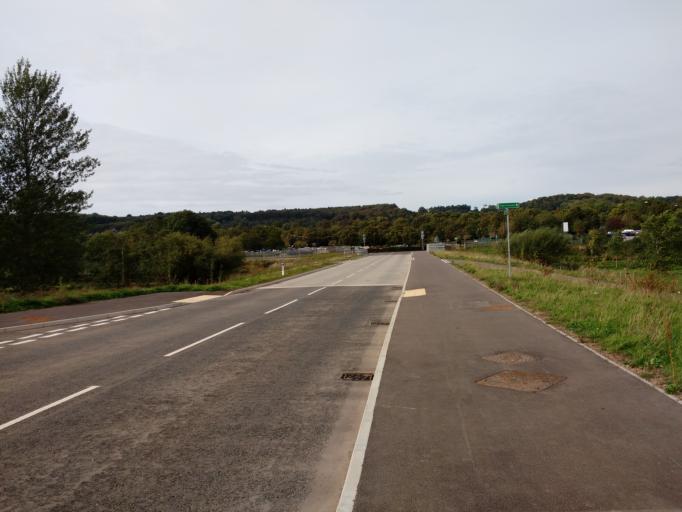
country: GB
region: England
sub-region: North Somerset
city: Long Ashton
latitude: 51.4347
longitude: -2.6336
